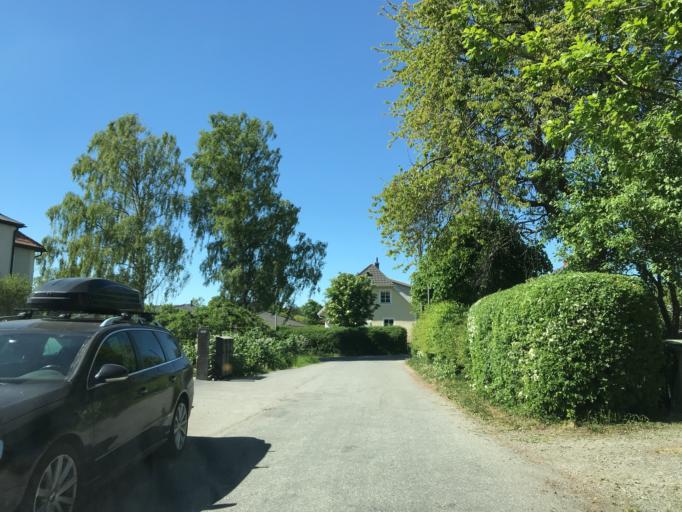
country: SE
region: Stockholm
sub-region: Sollentuna Kommun
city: Sollentuna
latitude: 59.4225
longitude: 17.9603
